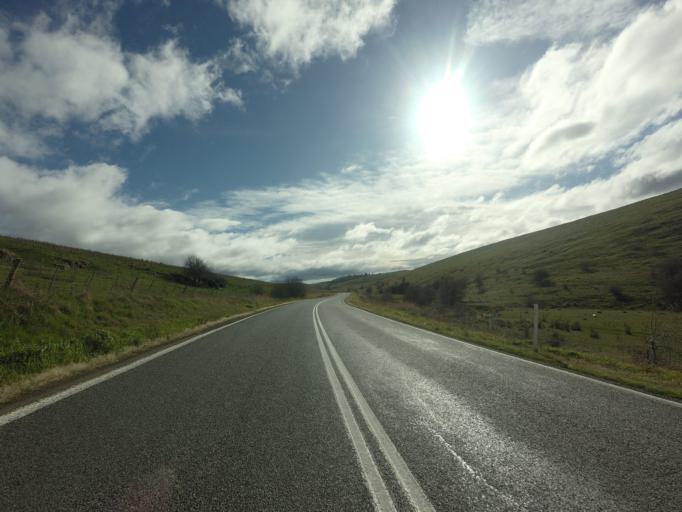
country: AU
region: Tasmania
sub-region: Derwent Valley
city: New Norfolk
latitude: -42.6420
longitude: 146.9193
